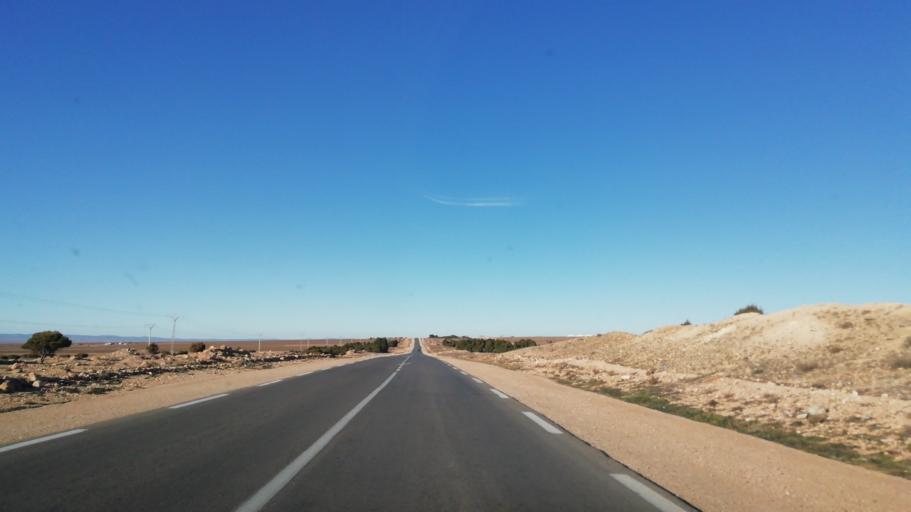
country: DZ
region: Tlemcen
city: Sebdou
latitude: 34.2479
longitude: -1.2572
